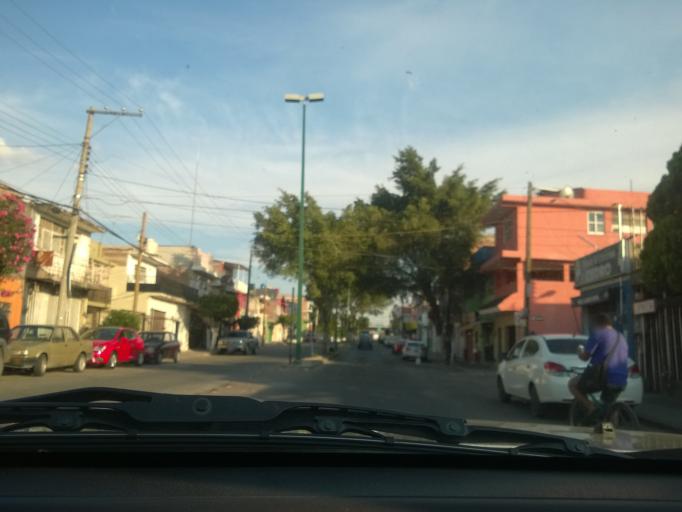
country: MX
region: Guanajuato
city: Leon
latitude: 21.1390
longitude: -101.6837
